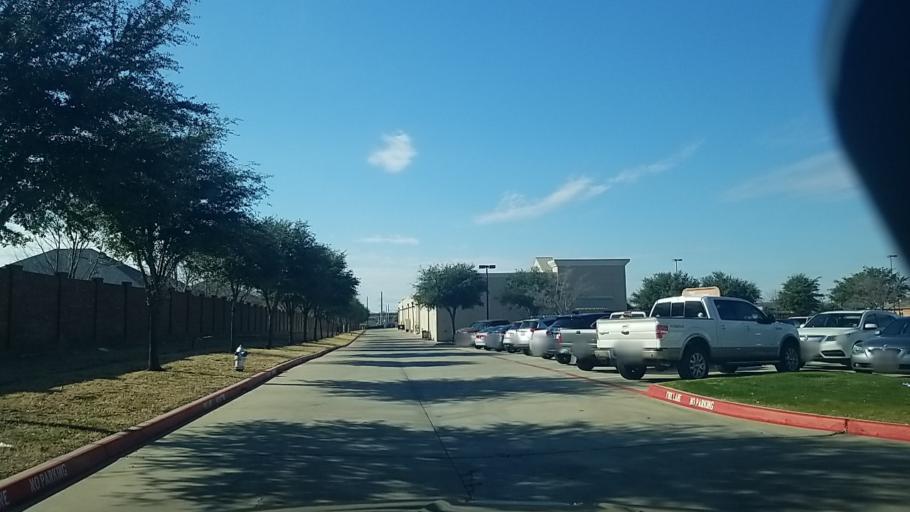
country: US
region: Texas
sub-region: Denton County
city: Corinth
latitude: 33.1450
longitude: -97.1024
